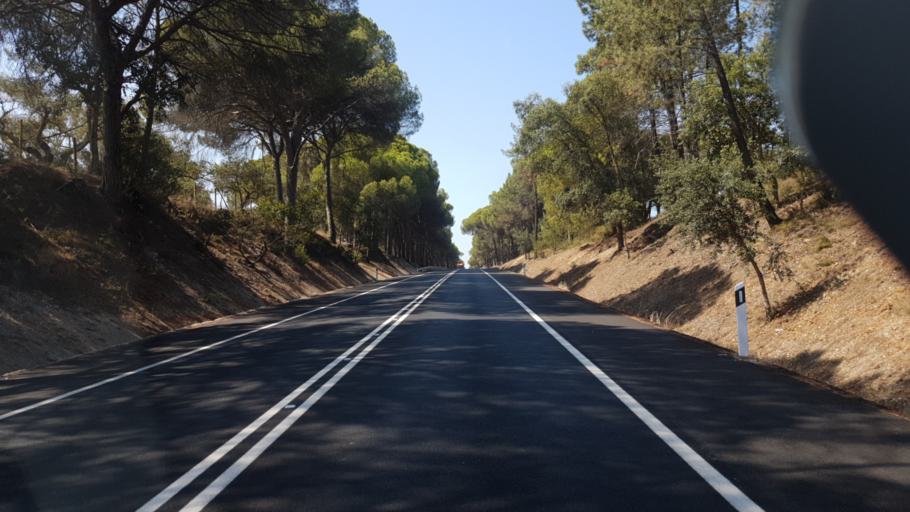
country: PT
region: Setubal
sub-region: Alcacer do Sal
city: Alcacer do Sal
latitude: 38.3373
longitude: -8.5209
